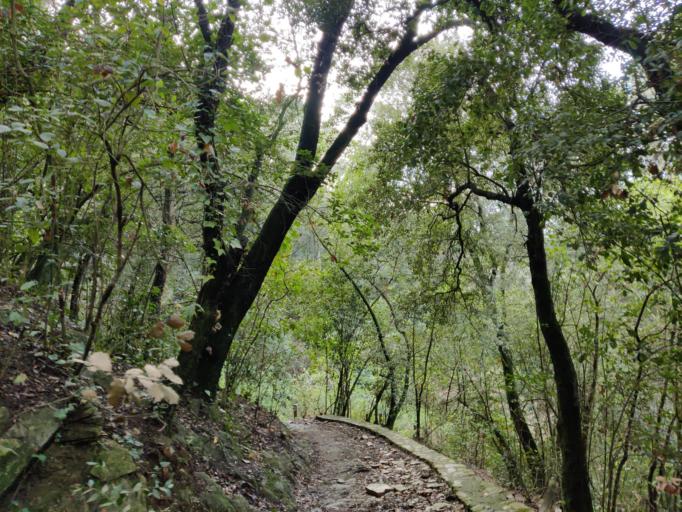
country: ES
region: Catalonia
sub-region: Provincia de Barcelona
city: Sarria-Sant Gervasi
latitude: 41.4198
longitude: 2.1125
